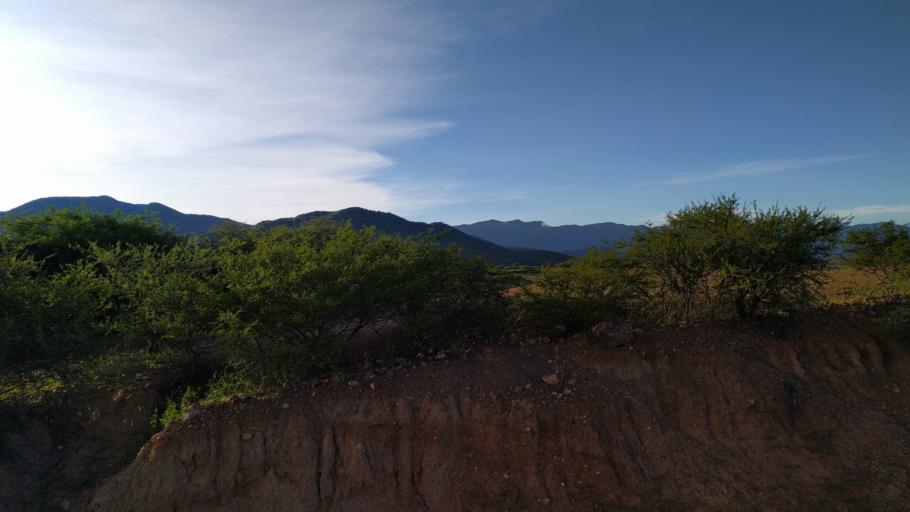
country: BO
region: Tarija
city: Tarija
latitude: -21.5217
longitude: -64.5659
